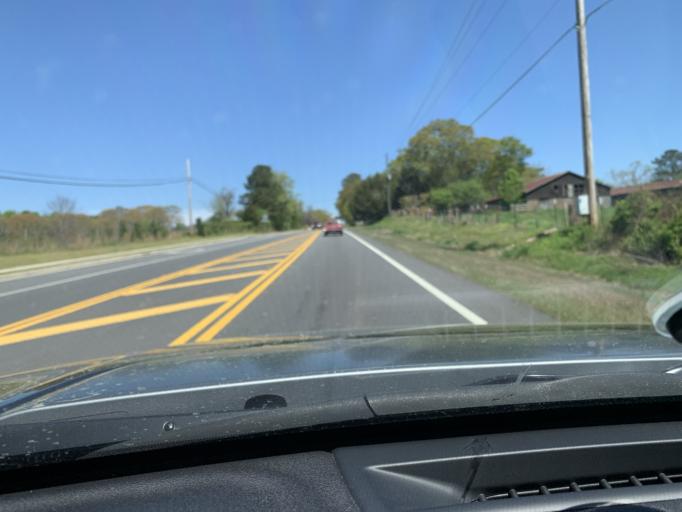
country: US
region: Georgia
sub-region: Fulton County
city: Milton
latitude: 34.1714
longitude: -84.2292
